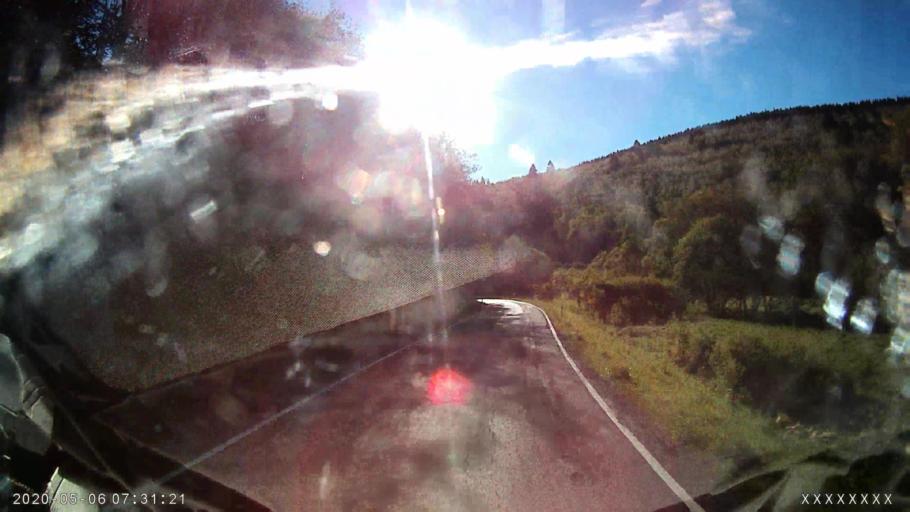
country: DE
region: Hesse
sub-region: Regierungsbezirk Giessen
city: Haiger
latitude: 50.8172
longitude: 8.2167
